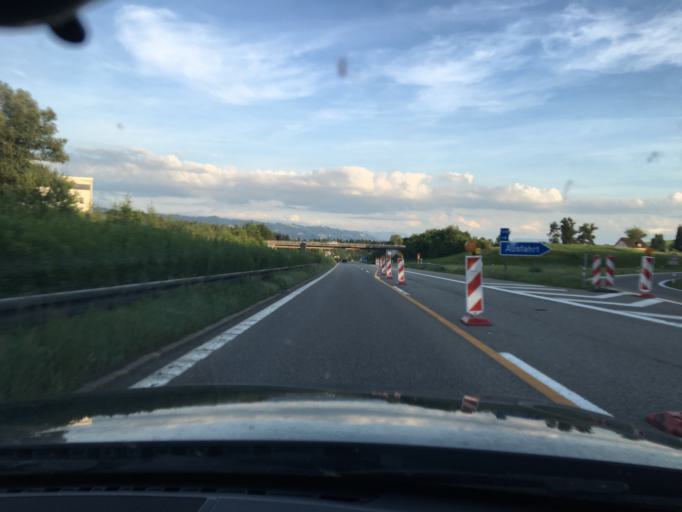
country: DE
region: Bavaria
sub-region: Swabia
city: Weissensberg
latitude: 47.5960
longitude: 9.7331
